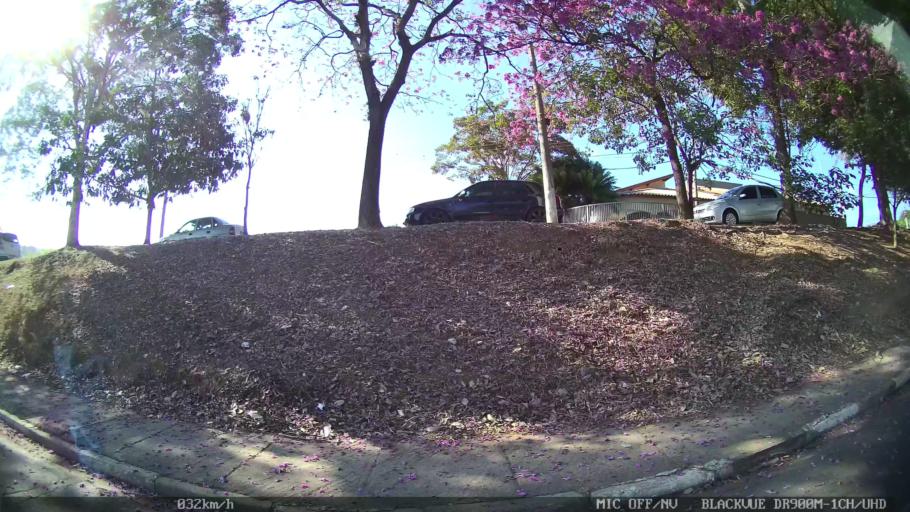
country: BR
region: Sao Paulo
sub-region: Campinas
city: Campinas
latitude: -22.9545
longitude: -47.1017
